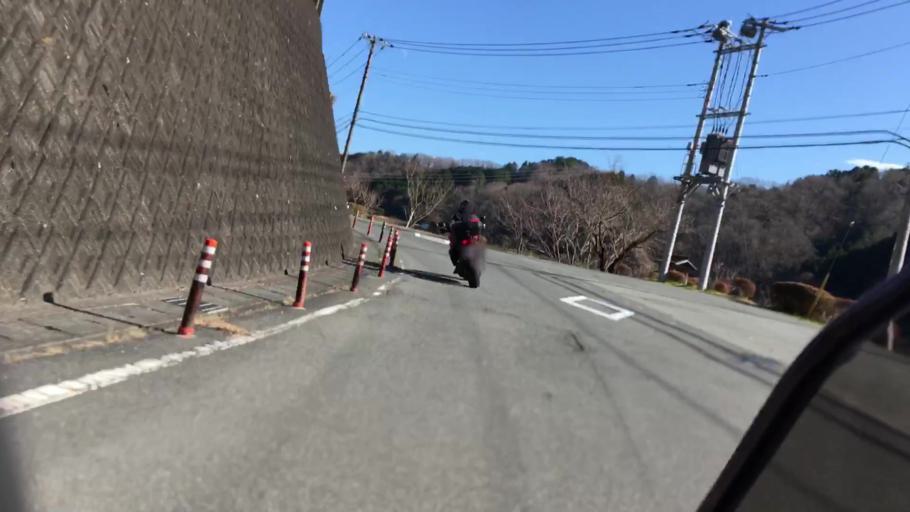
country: JP
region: Shizuoka
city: Ito
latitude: 34.9807
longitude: 138.9573
